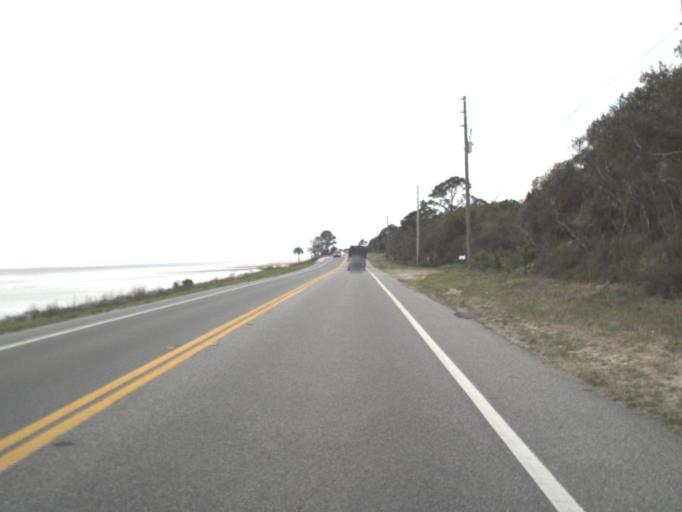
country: US
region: Florida
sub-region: Franklin County
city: Eastpoint
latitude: 29.7845
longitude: -84.7705
